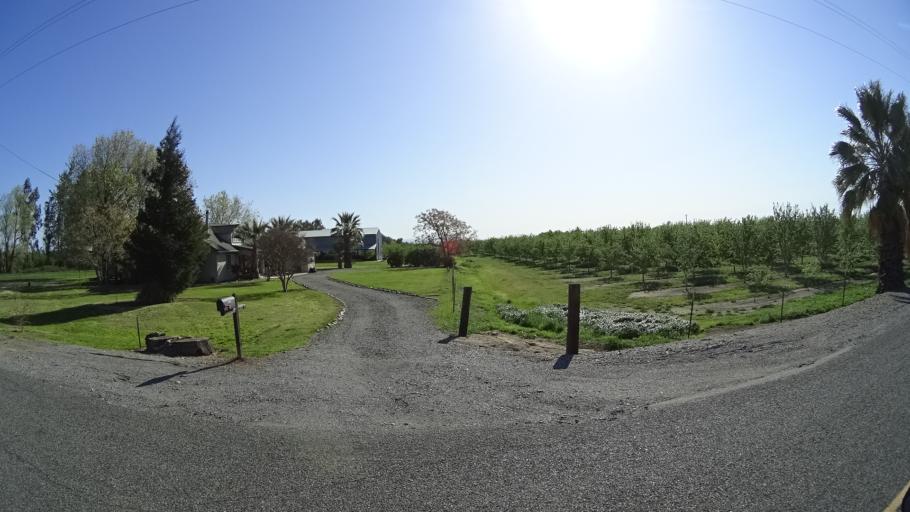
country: US
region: California
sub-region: Glenn County
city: Hamilton City
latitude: 39.7817
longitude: -122.0854
